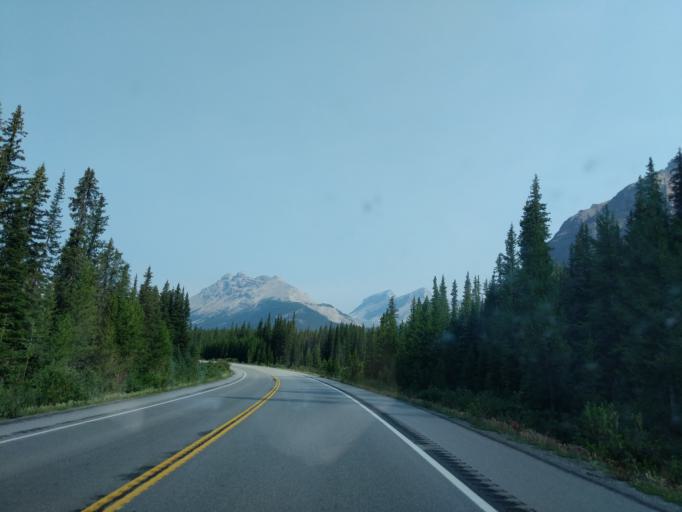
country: CA
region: Alberta
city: Lake Louise
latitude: 51.6191
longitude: -116.3168
